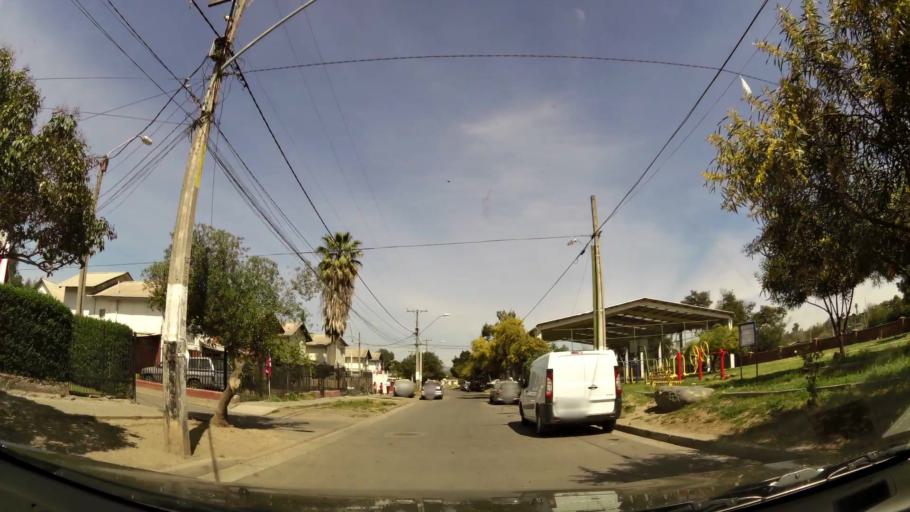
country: CL
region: Santiago Metropolitan
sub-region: Provincia de Cordillera
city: Puente Alto
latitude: -33.6286
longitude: -70.5769
